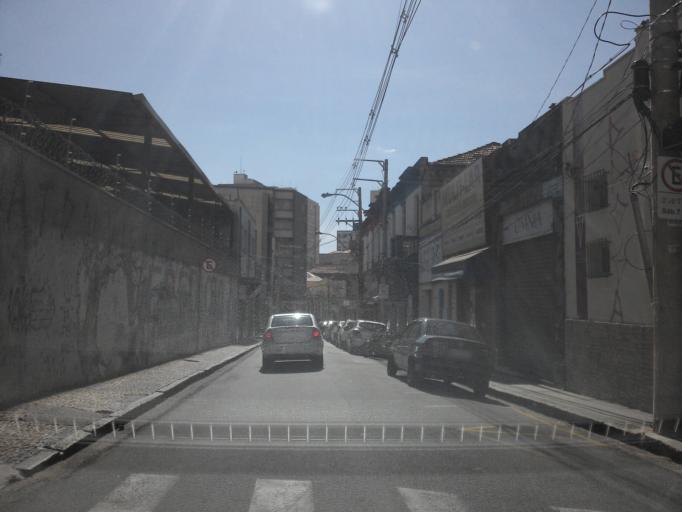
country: BR
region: Sao Paulo
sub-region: Campinas
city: Campinas
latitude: -22.9047
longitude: -47.0576
